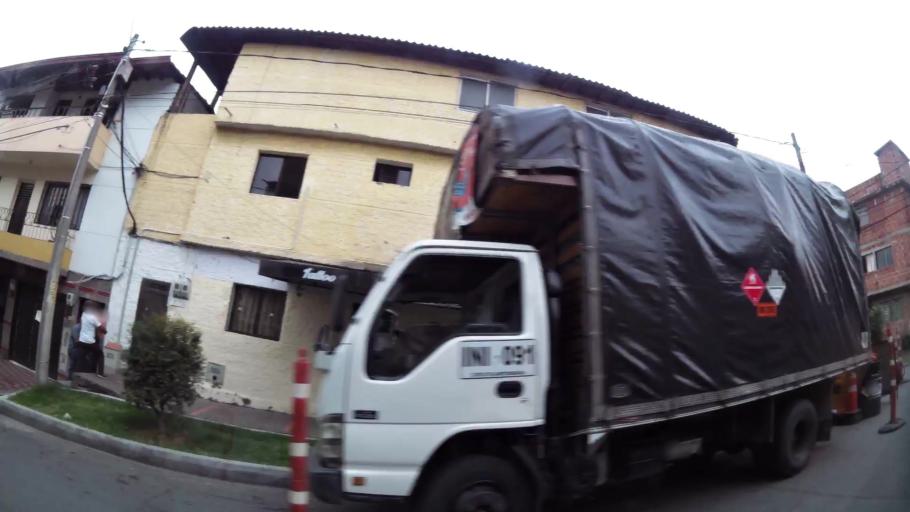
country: CO
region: Antioquia
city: Medellin
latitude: 6.2344
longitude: -75.5555
